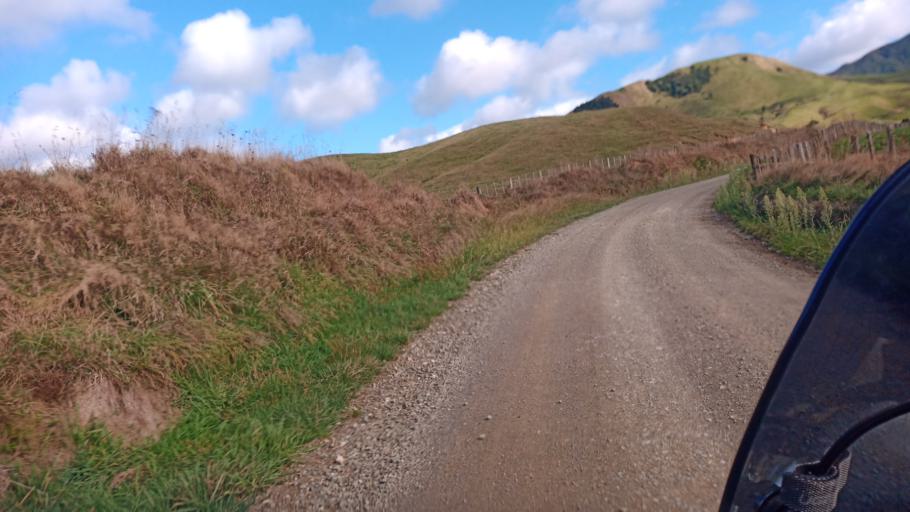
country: NZ
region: Bay of Plenty
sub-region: Opotiki District
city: Opotiki
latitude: -38.4565
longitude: 177.4039
